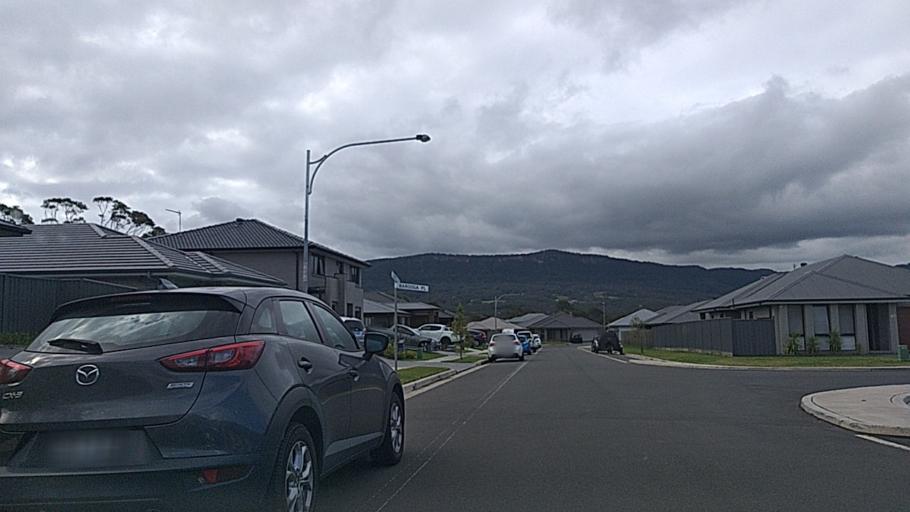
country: AU
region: New South Wales
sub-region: Wollongong
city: Dapto
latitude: -34.4870
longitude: 150.7654
